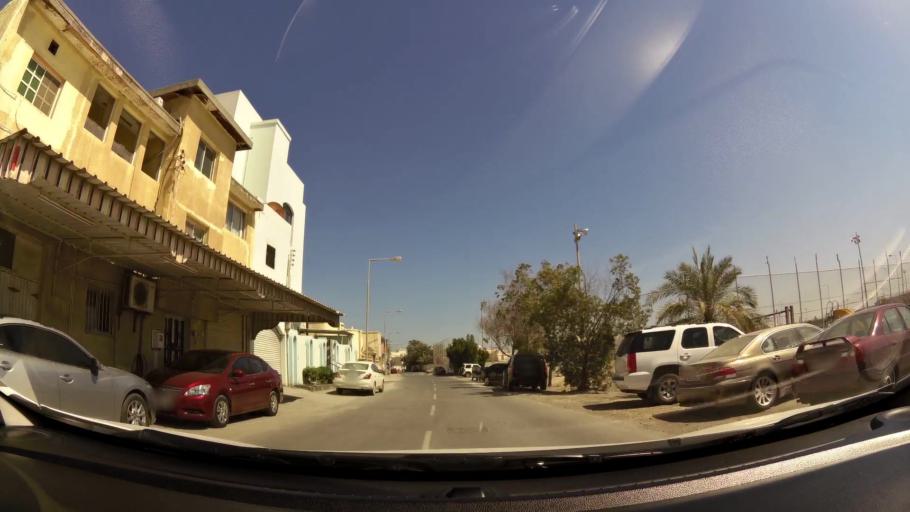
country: BH
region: Muharraq
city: Al Muharraq
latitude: 26.2782
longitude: 50.6341
